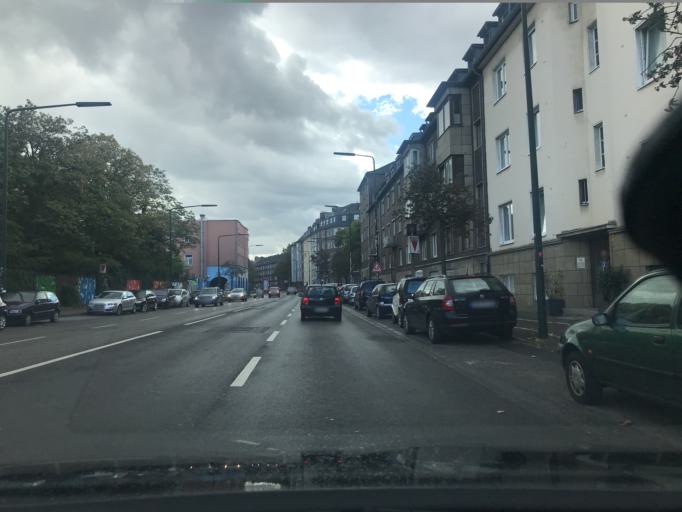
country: DE
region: North Rhine-Westphalia
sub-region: Regierungsbezirk Dusseldorf
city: Dusseldorf
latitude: 51.2422
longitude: 6.7872
